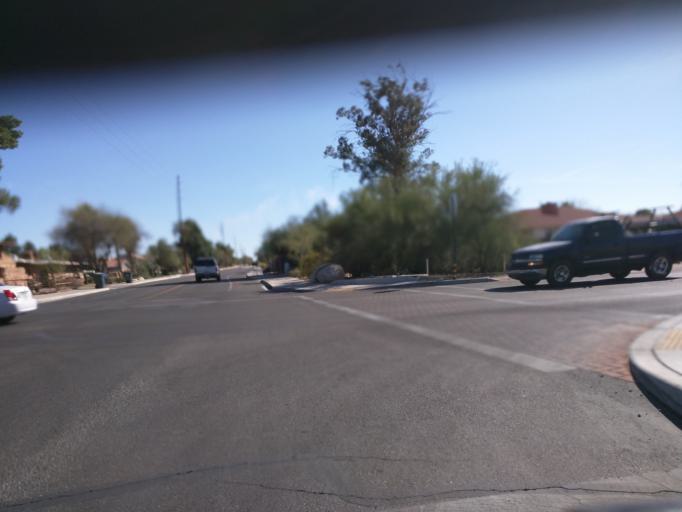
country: US
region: Arizona
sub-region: Pima County
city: Catalina Foothills
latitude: 32.2796
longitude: -110.9525
